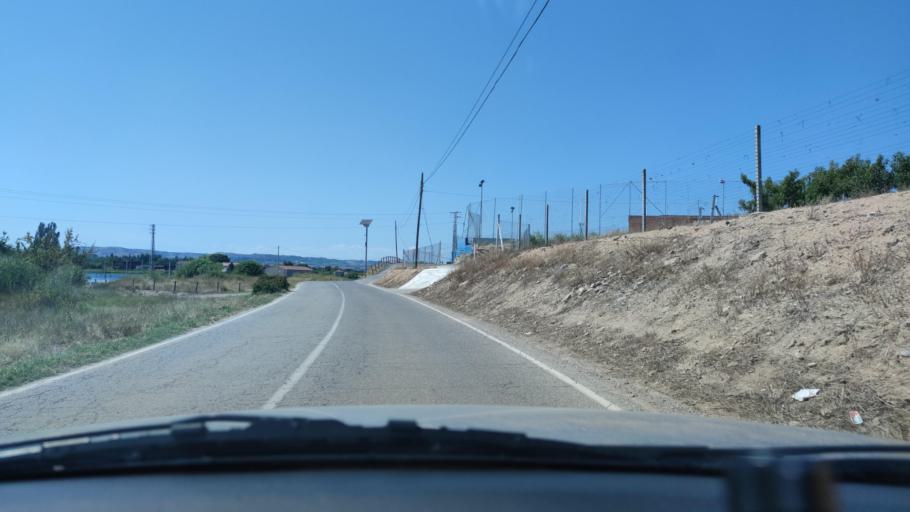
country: ES
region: Catalonia
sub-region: Provincia de Lleida
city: Lleida
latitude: 41.6414
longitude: 0.6249
